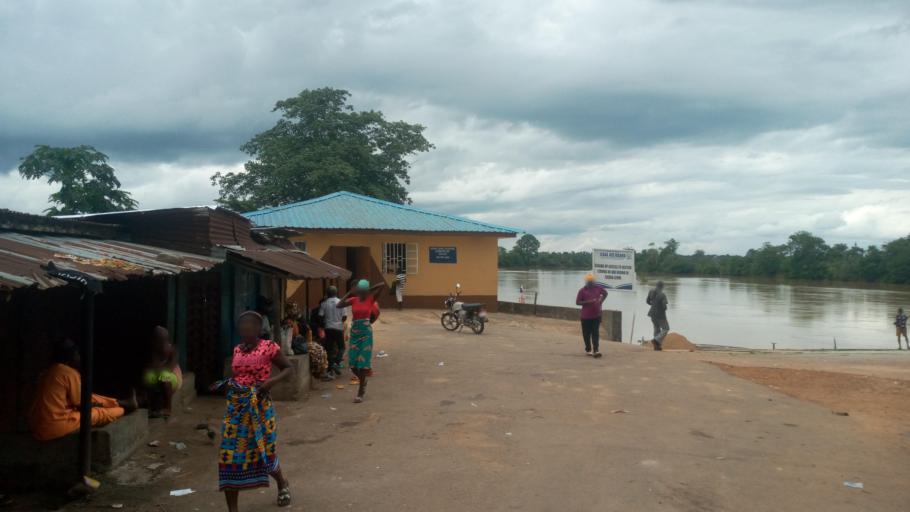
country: SL
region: Southern Province
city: Mogbwemo
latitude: 7.6039
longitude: -12.1804
